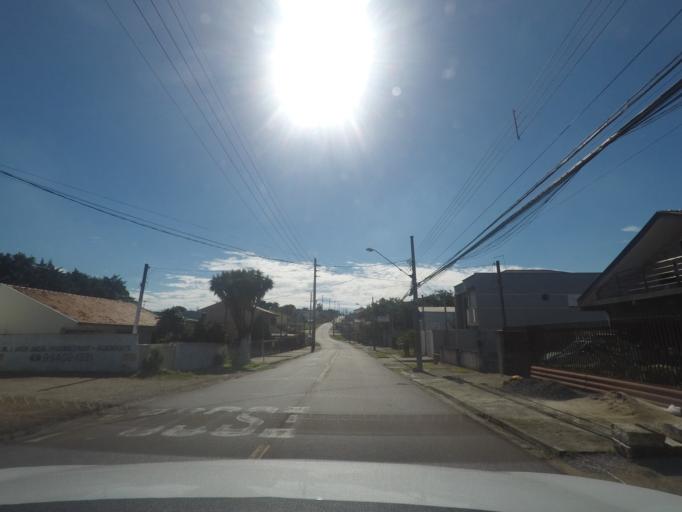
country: BR
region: Parana
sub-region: Sao Jose Dos Pinhais
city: Sao Jose dos Pinhais
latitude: -25.5062
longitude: -49.2787
